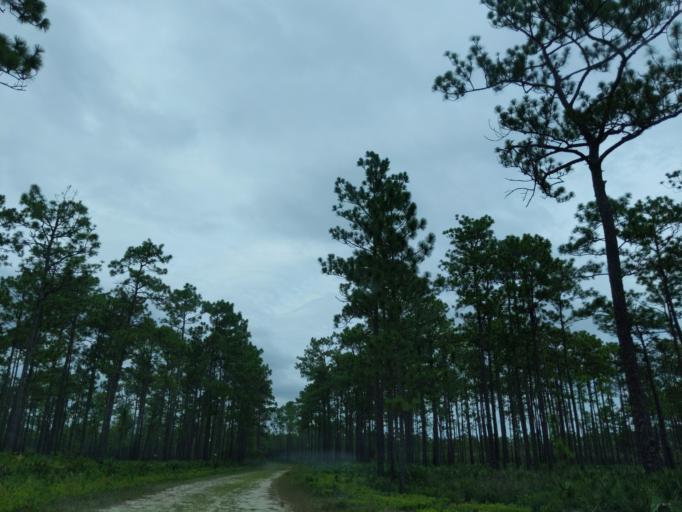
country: US
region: Florida
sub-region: Gadsden County
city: Midway
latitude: 30.3436
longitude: -84.4934
